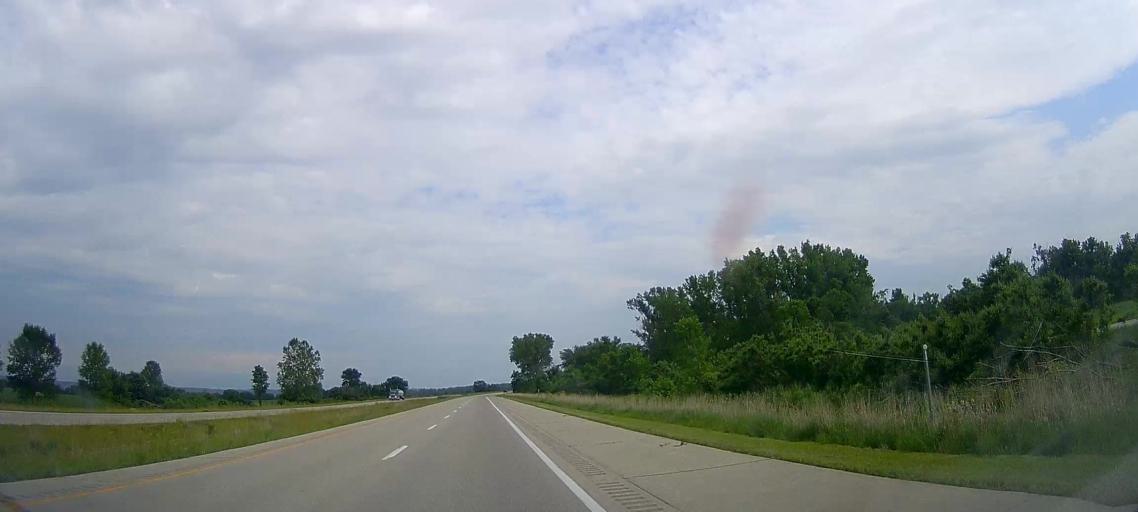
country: US
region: Nebraska
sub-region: Burt County
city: Tekamah
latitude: 41.8409
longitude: -96.0894
